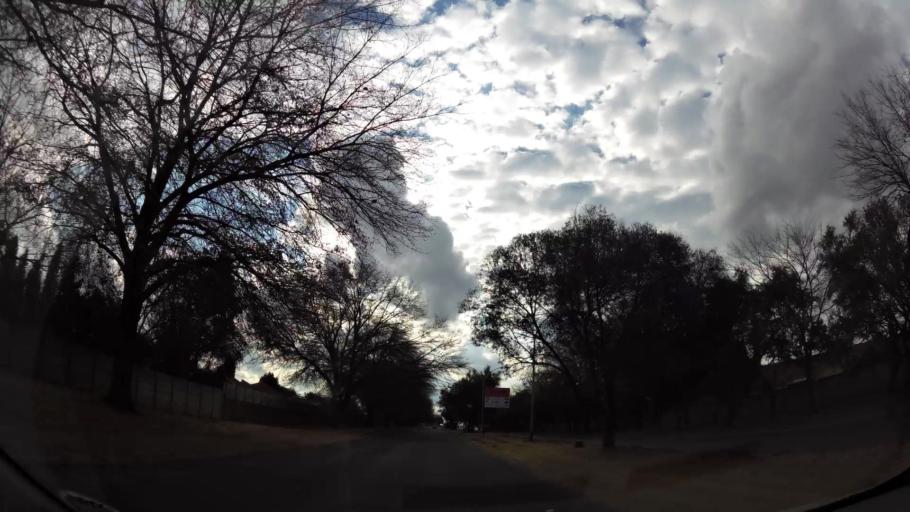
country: ZA
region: Orange Free State
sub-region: Fezile Dabi District Municipality
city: Sasolburg
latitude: -26.8011
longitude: 27.8098
